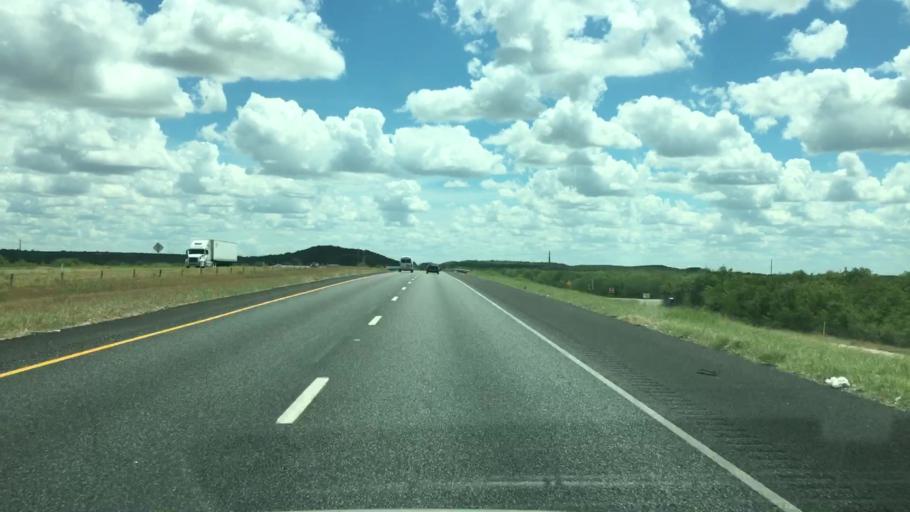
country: US
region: Texas
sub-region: Live Oak County
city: Three Rivers
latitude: 28.7357
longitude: -98.2901
